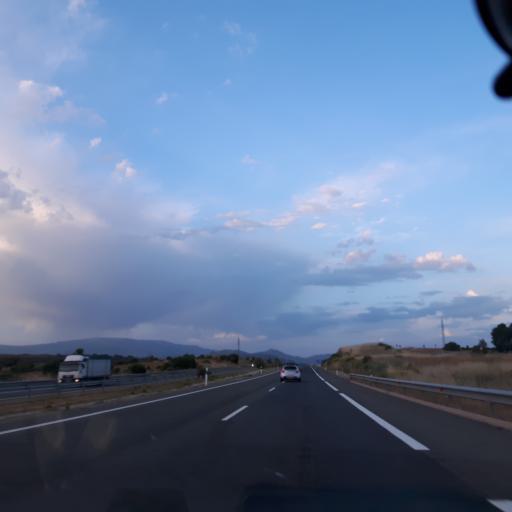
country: ES
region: Castille and Leon
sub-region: Provincia de Salamanca
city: Guijuelo
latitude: 40.5385
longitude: -5.6631
